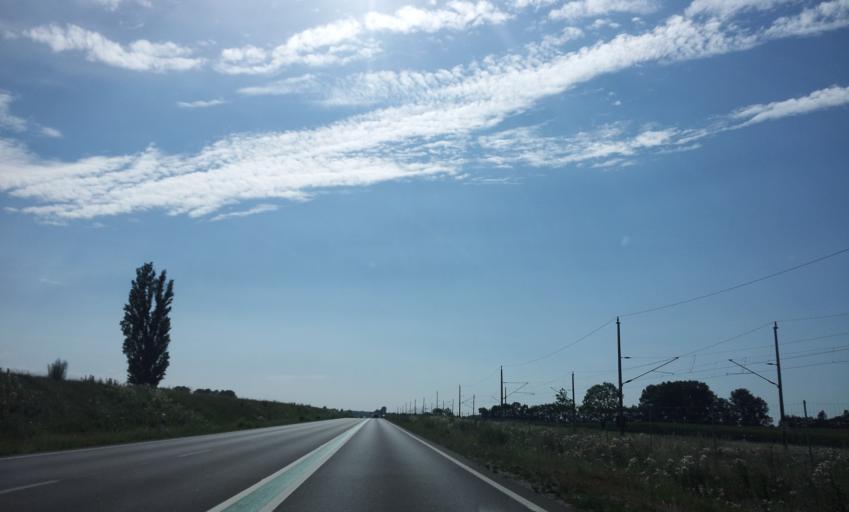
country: DE
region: Mecklenburg-Vorpommern
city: Rambin
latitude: 54.3506
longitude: 13.1894
